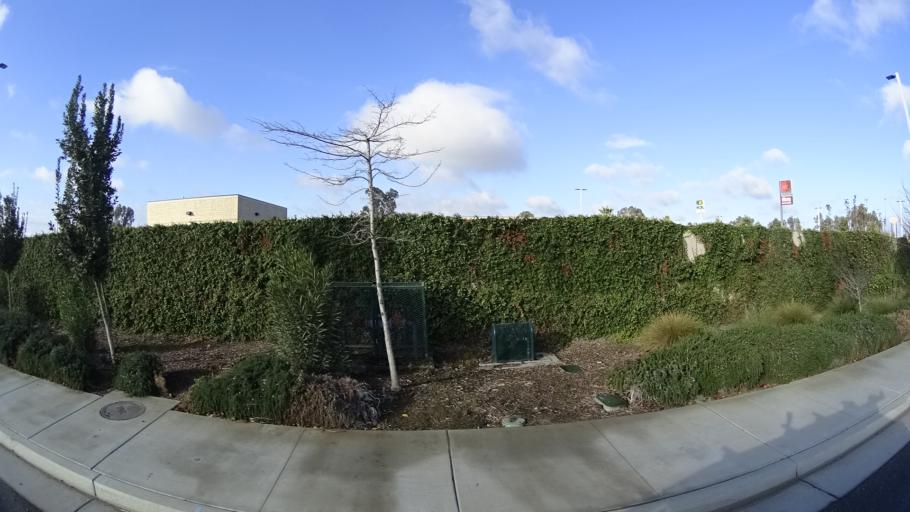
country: US
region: California
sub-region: Kern County
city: Greenfield
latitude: 35.2931
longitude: -119.0272
